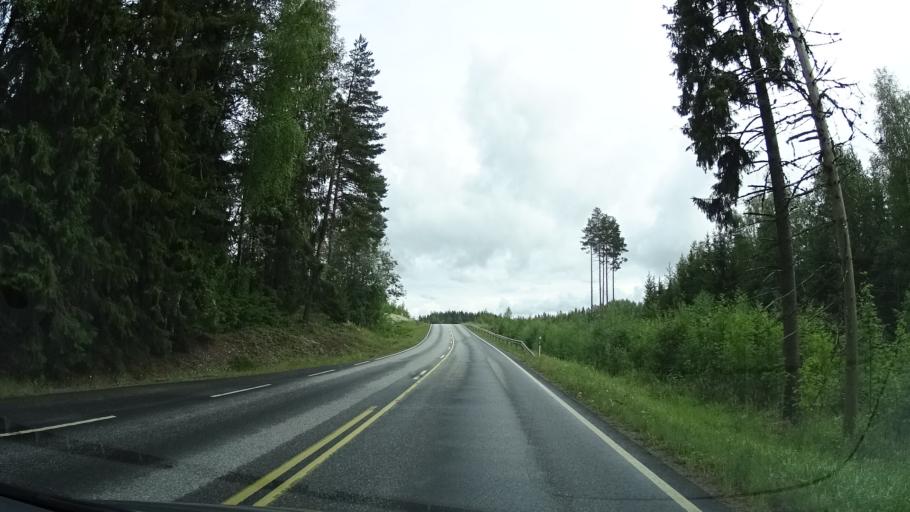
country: FI
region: Haeme
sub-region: Forssa
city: Humppila
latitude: 61.0971
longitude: 23.3470
